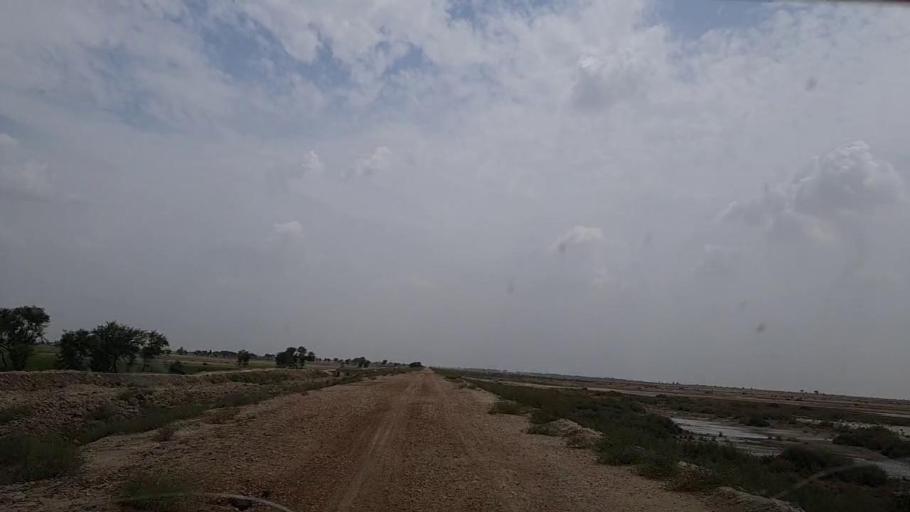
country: PK
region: Sindh
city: Johi
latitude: 26.7876
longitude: 67.5997
